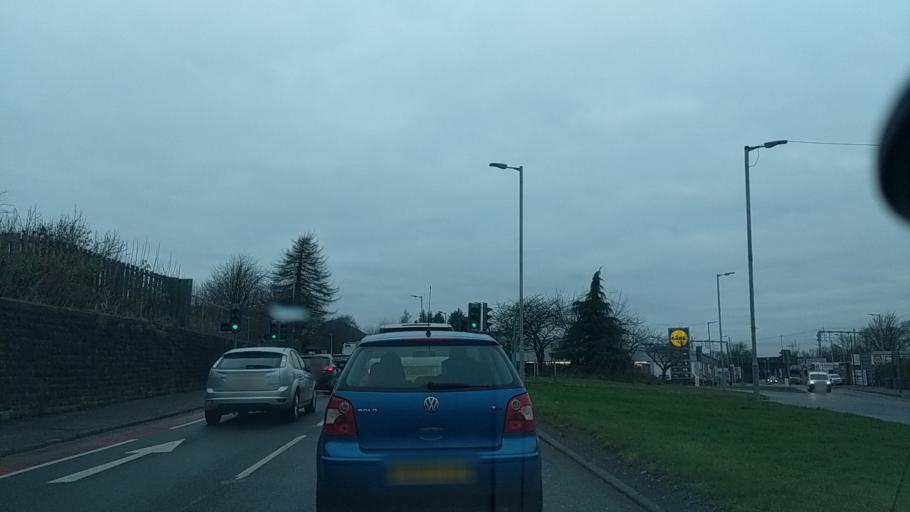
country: GB
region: Scotland
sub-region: South Lanarkshire
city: Rutherglen
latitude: 55.8264
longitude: -4.1933
